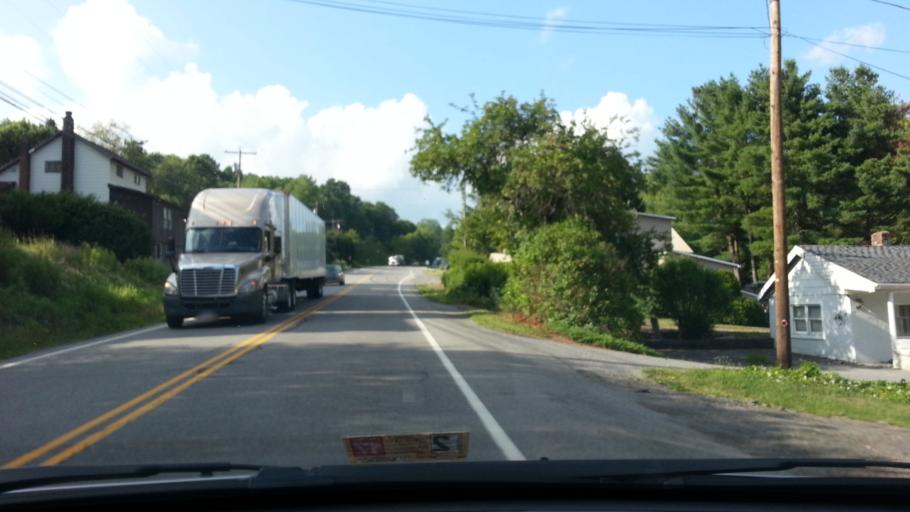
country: US
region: Pennsylvania
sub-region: Elk County
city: Saint Marys
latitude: 41.2933
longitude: -78.5044
